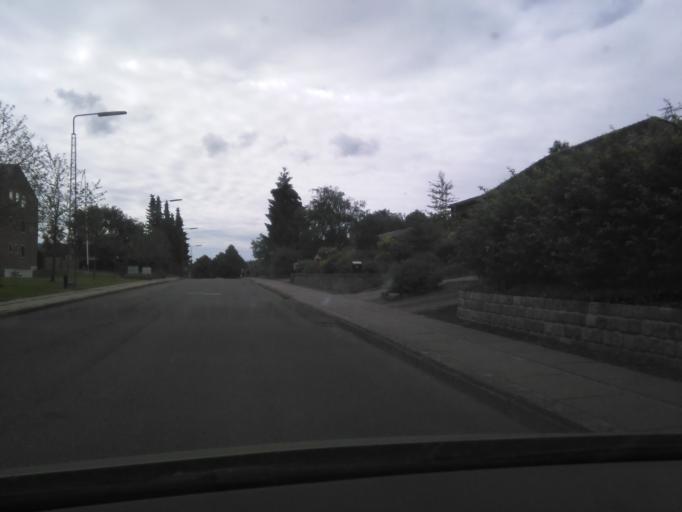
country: DK
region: Central Jutland
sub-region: Odder Kommune
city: Odder
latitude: 55.9770
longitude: 10.1477
